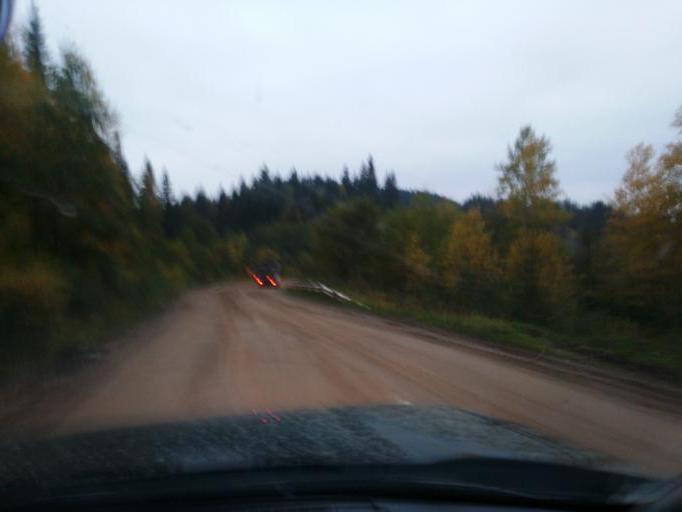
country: RU
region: Sverdlovsk
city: Sylva
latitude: 57.7990
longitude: 58.5418
